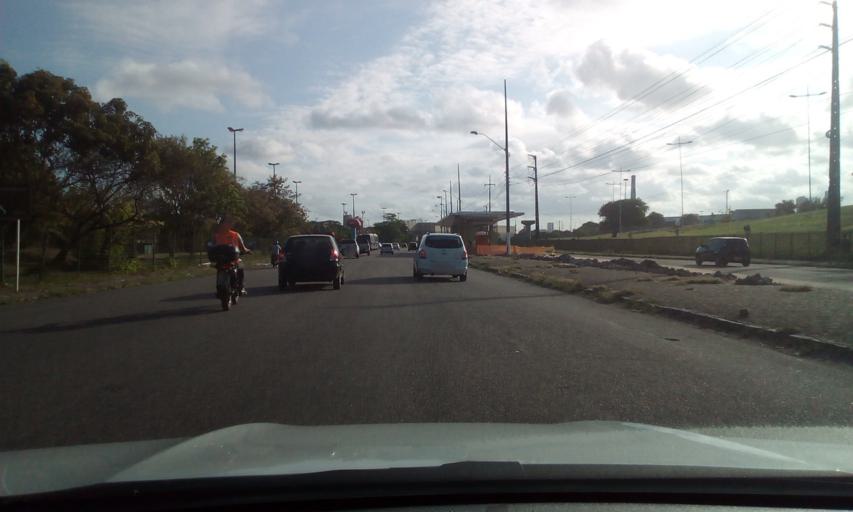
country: BR
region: Pernambuco
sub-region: Recife
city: Recife
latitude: -8.0320
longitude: -34.8678
